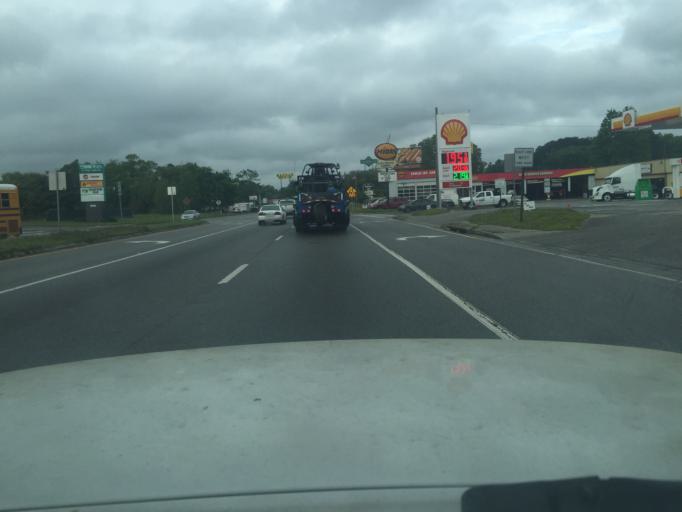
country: US
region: Georgia
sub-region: Chatham County
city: Savannah
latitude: 32.0536
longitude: -81.1433
